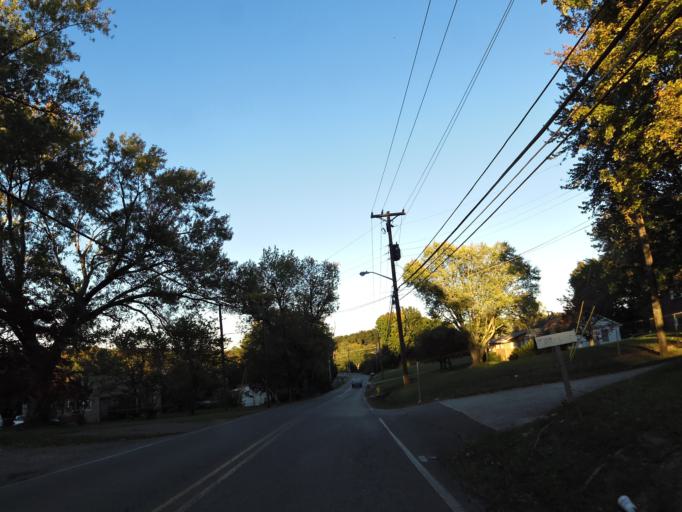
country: US
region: Tennessee
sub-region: Knox County
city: Knoxville
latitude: 36.0151
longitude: -83.9885
